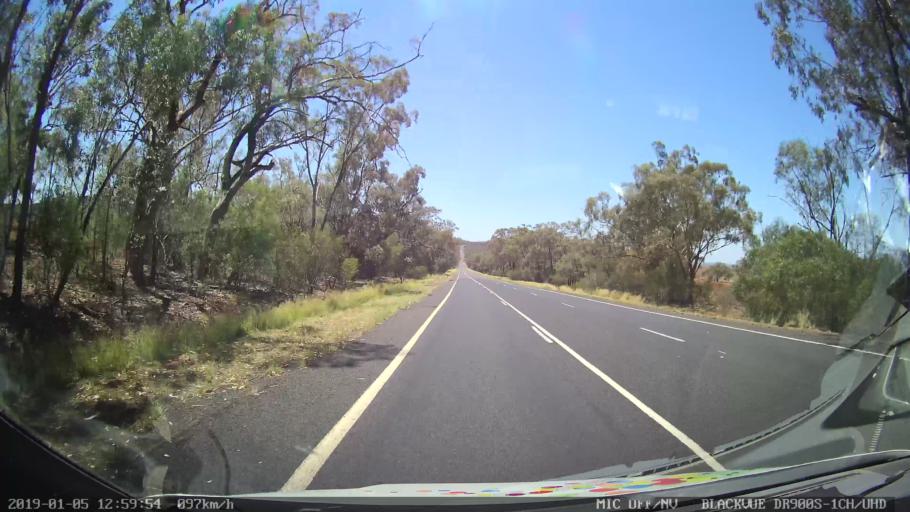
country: AU
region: New South Wales
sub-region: Narrabri
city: Boggabri
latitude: -31.1157
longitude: 149.7728
